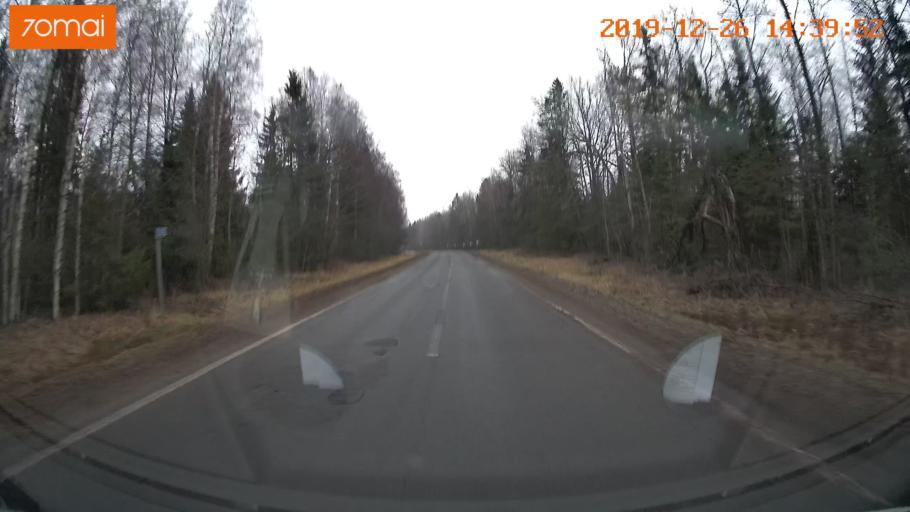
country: RU
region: Jaroslavl
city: Poshekhon'ye
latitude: 58.3795
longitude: 38.9869
